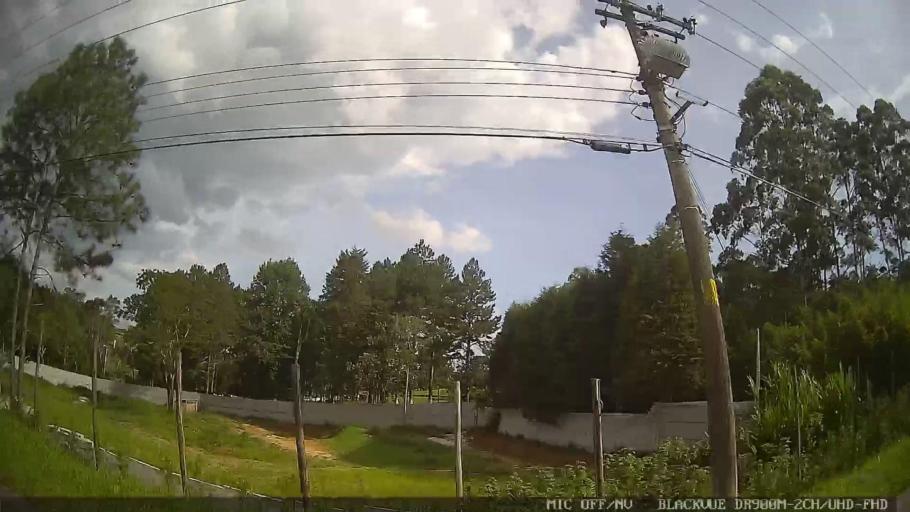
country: BR
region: Sao Paulo
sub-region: Mogi das Cruzes
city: Mogi das Cruzes
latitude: -23.6093
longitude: -46.1720
